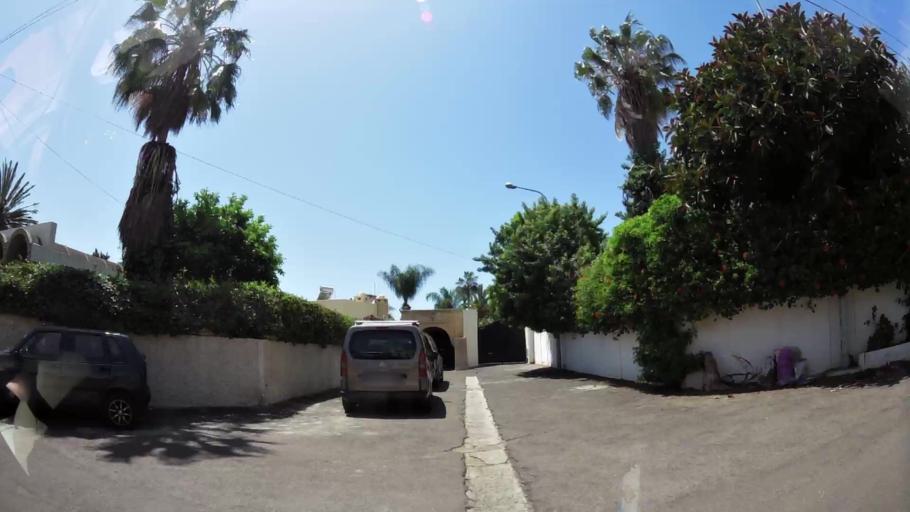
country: MA
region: Souss-Massa-Draa
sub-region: Agadir-Ida-ou-Tnan
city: Agadir
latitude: 30.4289
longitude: -9.5942
